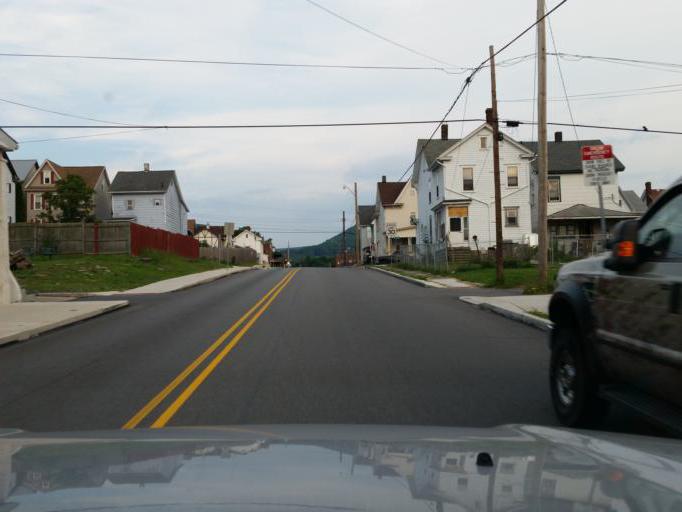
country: US
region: Pennsylvania
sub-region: Blair County
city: Altoona
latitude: 40.5232
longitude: -78.3849
